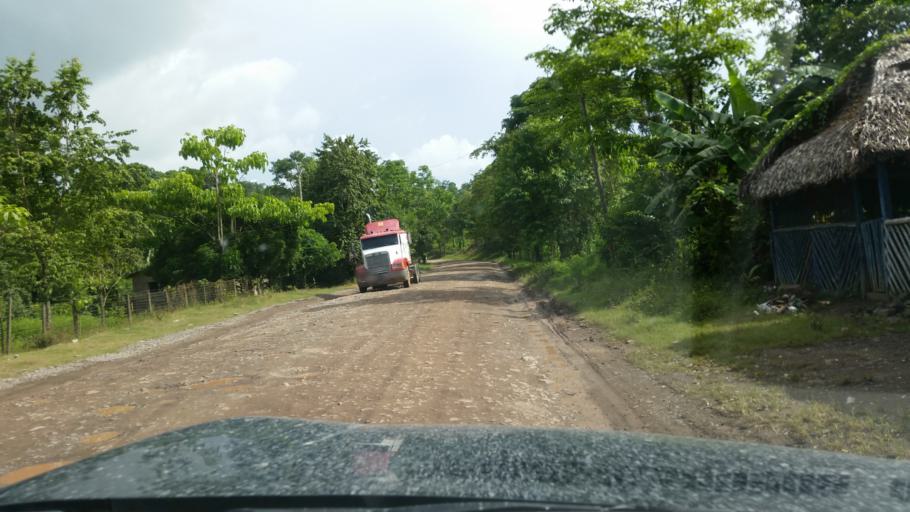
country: NI
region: Atlantico Norte (RAAN)
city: Siuna
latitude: 13.6316
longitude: -84.7950
